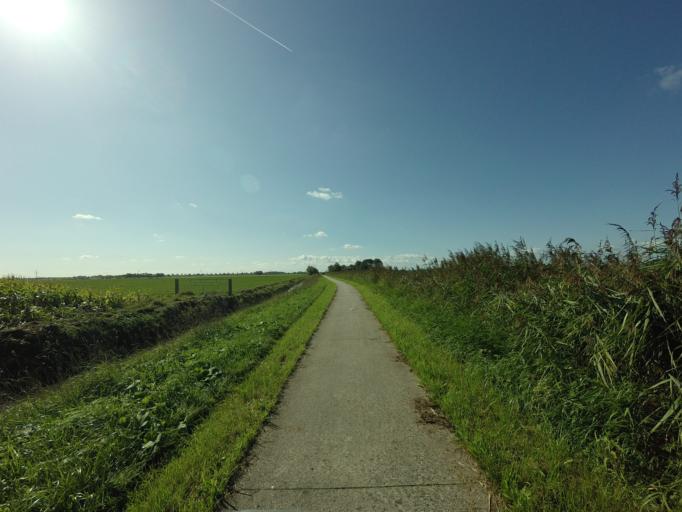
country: NL
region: Friesland
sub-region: Gemeente Boarnsterhim
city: Reduzum
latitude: 53.1316
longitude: 5.7566
